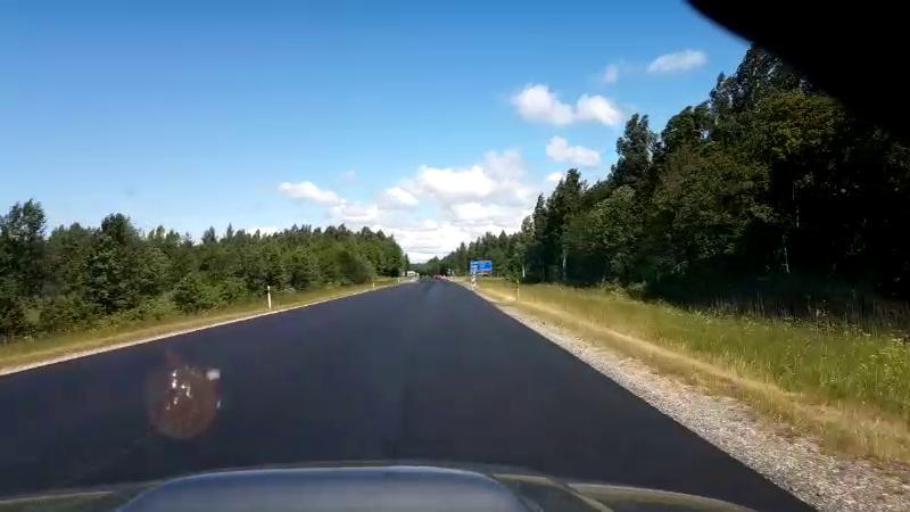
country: LV
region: Salacgrivas
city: Ainazi
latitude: 58.0112
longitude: 24.4914
